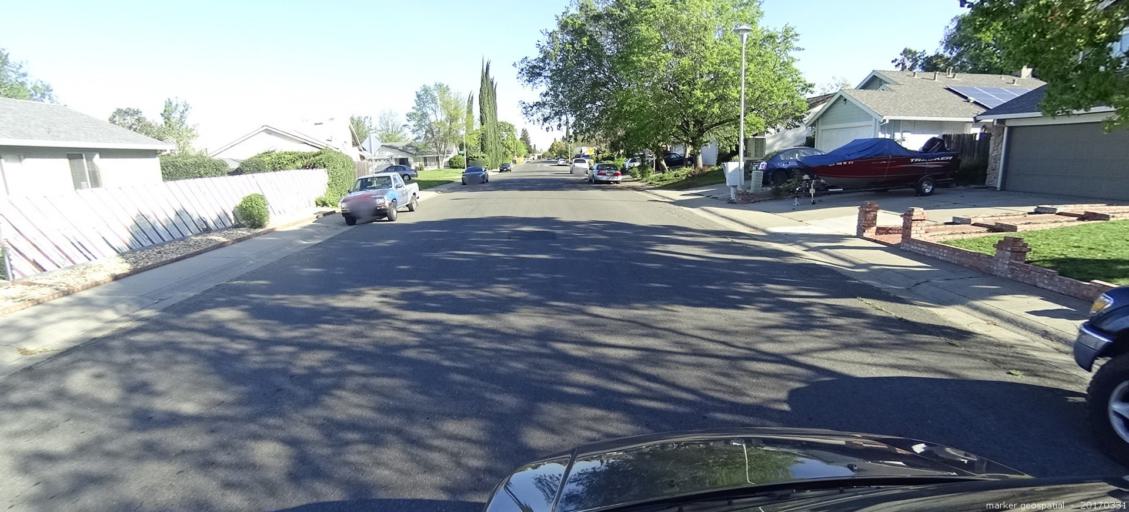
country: US
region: California
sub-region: Sacramento County
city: Parkway
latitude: 38.4664
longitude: -121.4570
